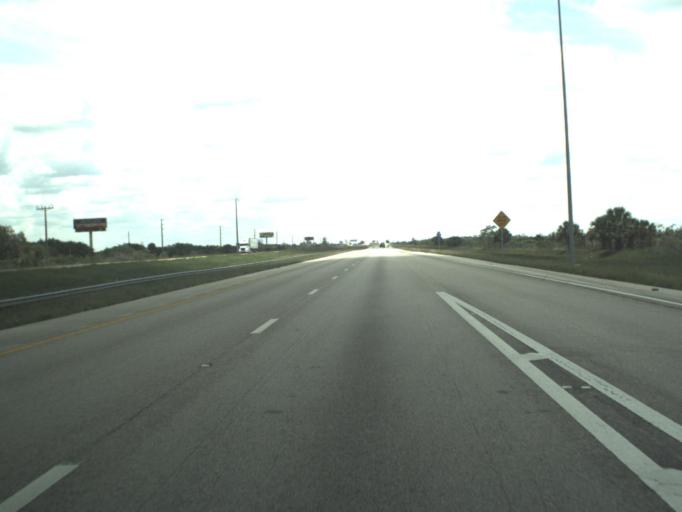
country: US
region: Florida
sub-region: Broward County
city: Weston
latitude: 26.1697
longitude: -80.8506
